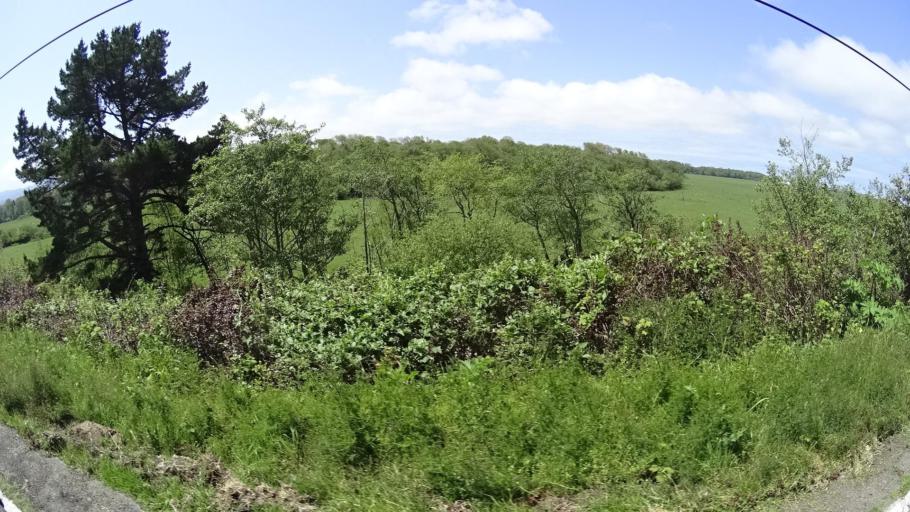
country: US
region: California
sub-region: Humboldt County
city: Ferndale
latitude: 40.6295
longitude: -124.2214
